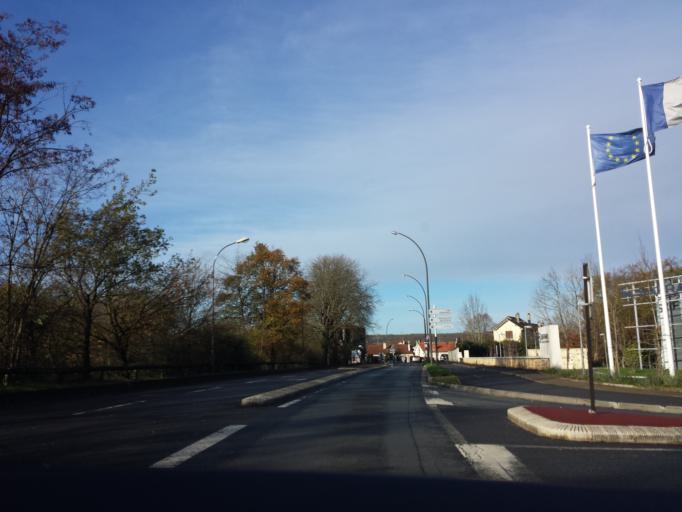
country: FR
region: Ile-de-France
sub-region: Departement de l'Essonne
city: Palaiseau
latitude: 48.7308
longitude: 2.2447
